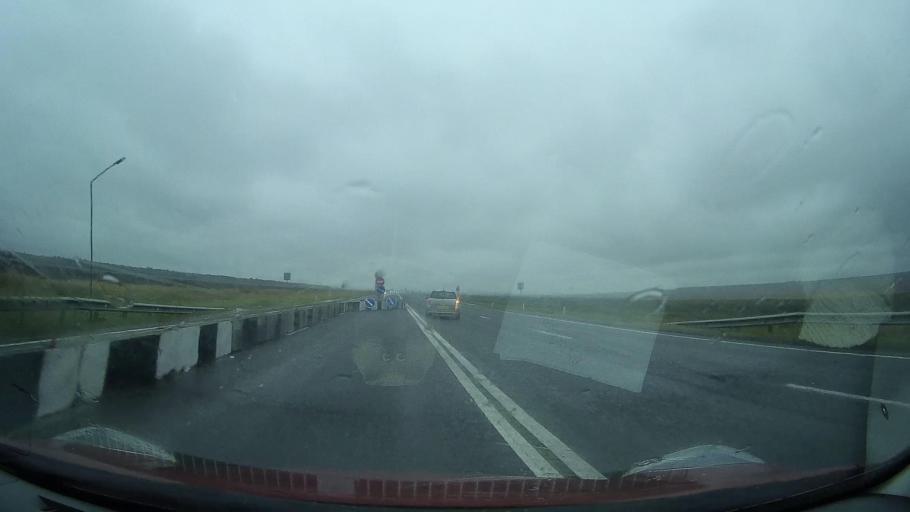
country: RU
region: Stavropol'skiy
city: Nevinnomyssk
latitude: 44.6258
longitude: 42.0564
